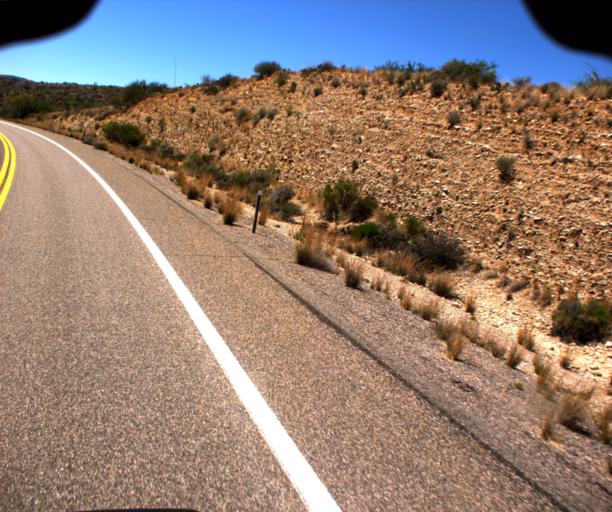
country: US
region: Arizona
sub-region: Yavapai County
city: Bagdad
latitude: 34.5251
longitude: -113.1185
